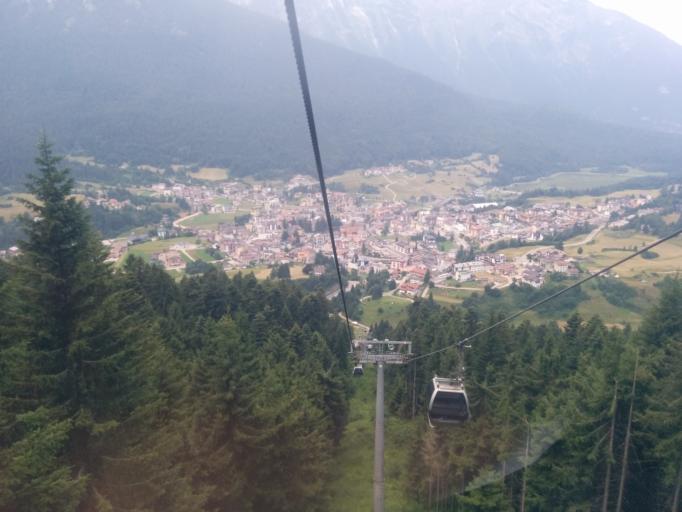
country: IT
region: Trentino-Alto Adige
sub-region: Provincia di Trento
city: Andalo
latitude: 46.1566
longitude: 11.0117
